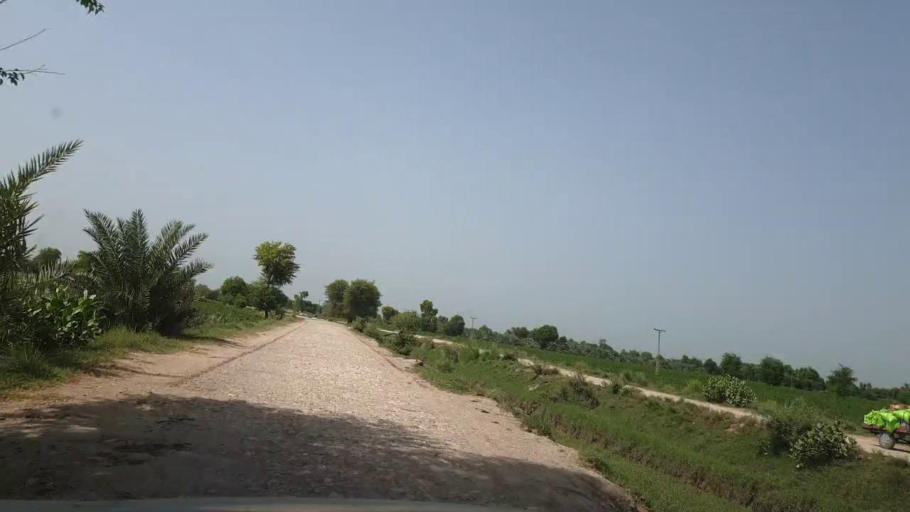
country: PK
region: Sindh
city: Pano Aqil
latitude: 27.8343
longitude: 69.1853
